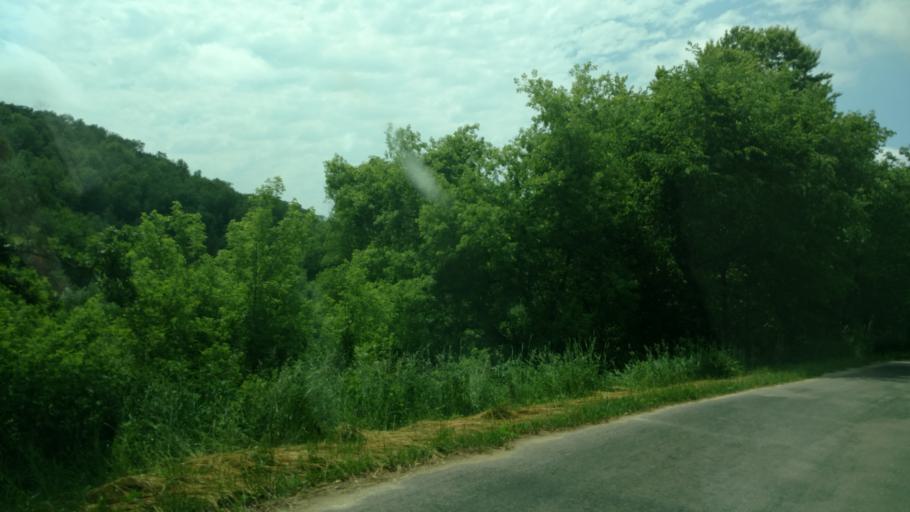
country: US
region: Wisconsin
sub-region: Monroe County
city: Cashton
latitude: 43.7206
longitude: -90.6759
